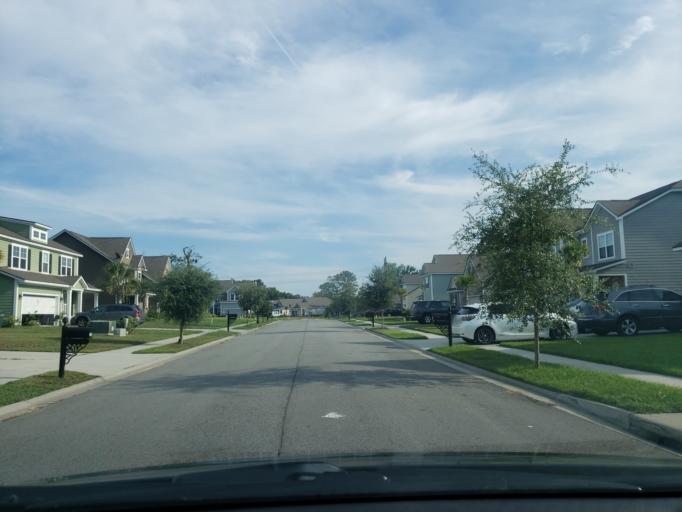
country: US
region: Georgia
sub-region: Chatham County
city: Montgomery
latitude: 31.9558
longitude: -81.1559
